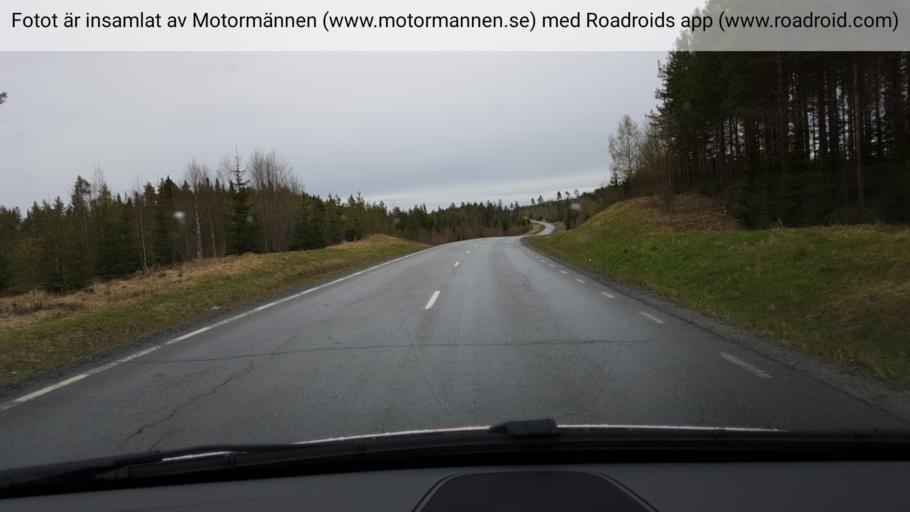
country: SE
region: Jaemtland
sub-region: Krokoms Kommun
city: Krokom
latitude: 63.2769
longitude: 14.4408
